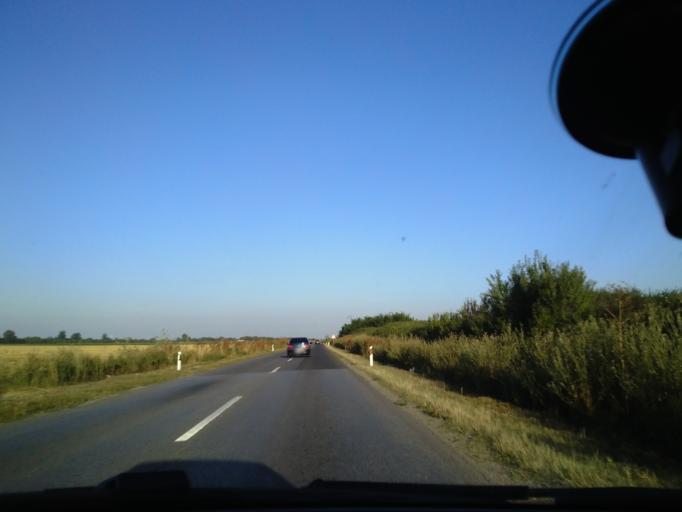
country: RS
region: Autonomna Pokrajina Vojvodina
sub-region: Juznobacki Okrug
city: Backi Petrovac
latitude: 45.3418
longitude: 19.6475
